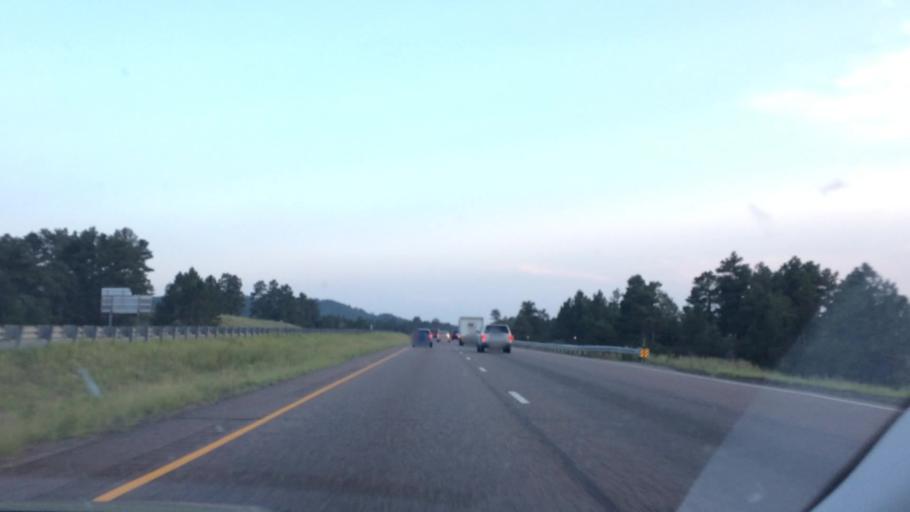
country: US
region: Colorado
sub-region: Douglas County
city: Perry Park
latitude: 39.2382
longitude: -104.8774
